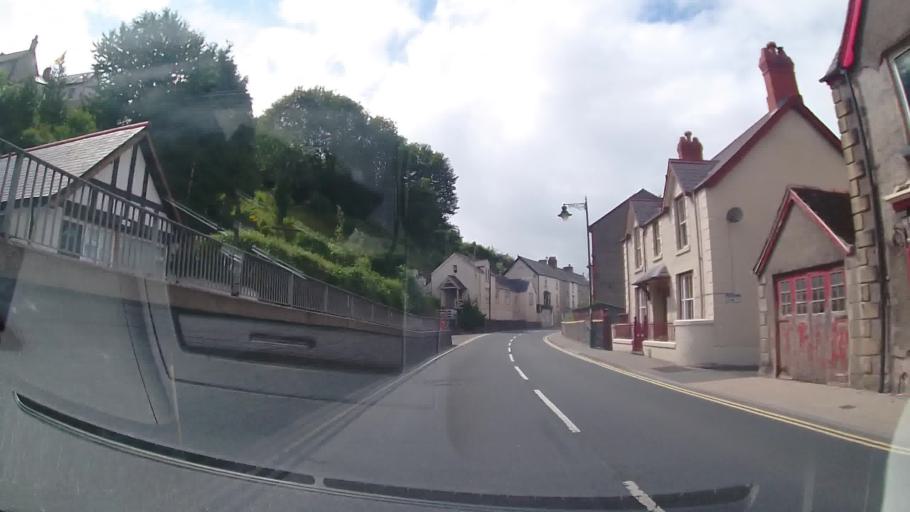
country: GB
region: Wales
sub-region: Denbighshire
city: Corwen
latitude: 52.9799
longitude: -3.3758
